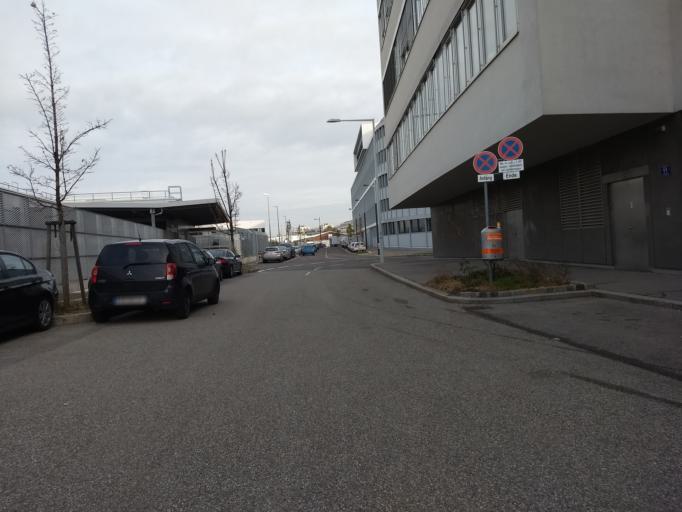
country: AT
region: Vienna
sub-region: Wien Stadt
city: Vienna
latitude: 48.2474
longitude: 16.3660
